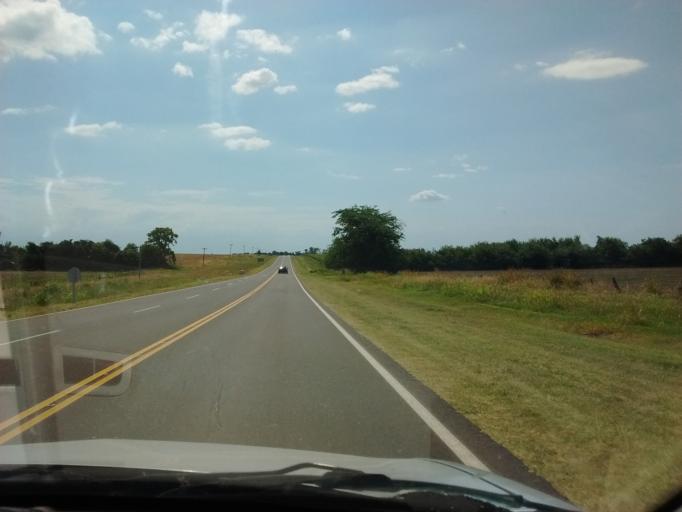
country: AR
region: Entre Rios
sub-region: Departamento de Victoria
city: Victoria
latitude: -32.6466
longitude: -60.0959
